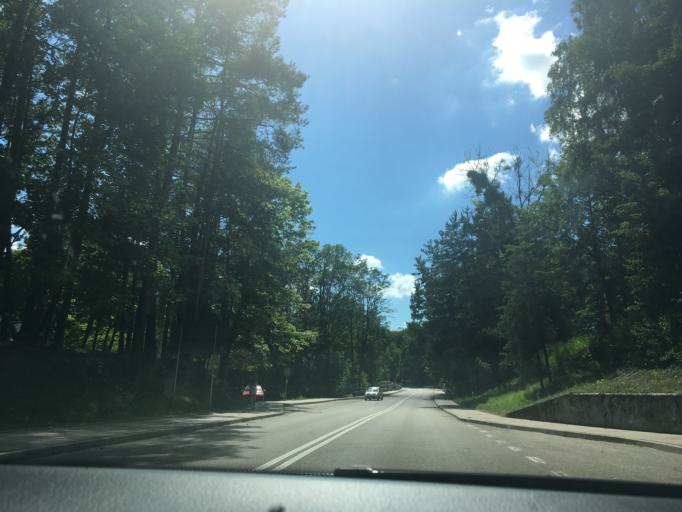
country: PL
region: Podlasie
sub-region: Powiat augustowski
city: Augustow
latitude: 53.8683
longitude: 23.0937
